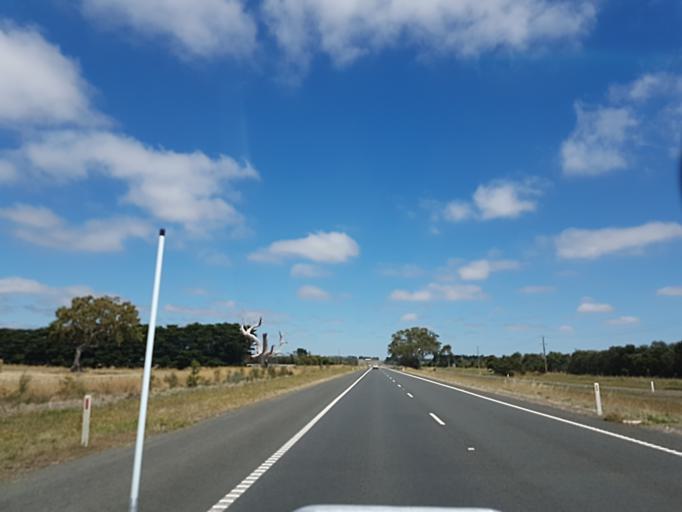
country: AU
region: Victoria
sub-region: Greater Geelong
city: Wandana Heights
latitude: -38.2136
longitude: 144.1457
